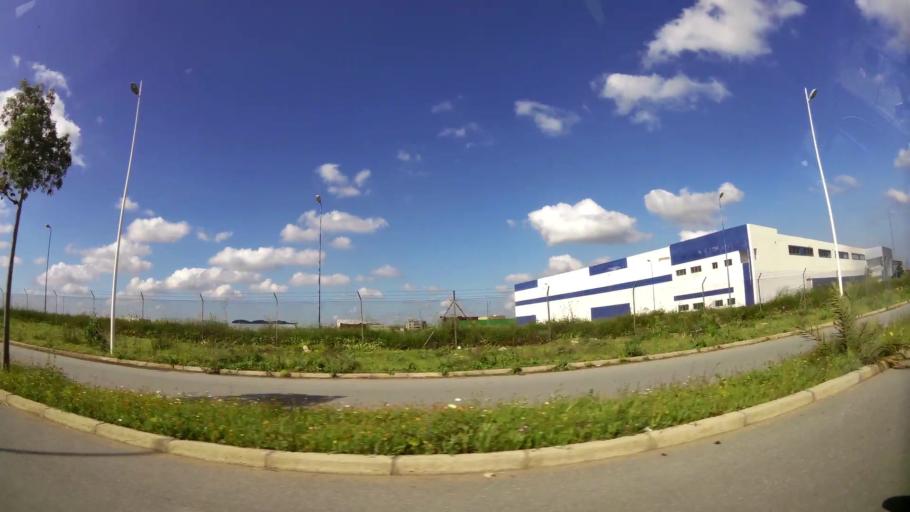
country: MA
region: Grand Casablanca
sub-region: Mediouna
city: Mediouna
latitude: 33.3894
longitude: -7.5407
